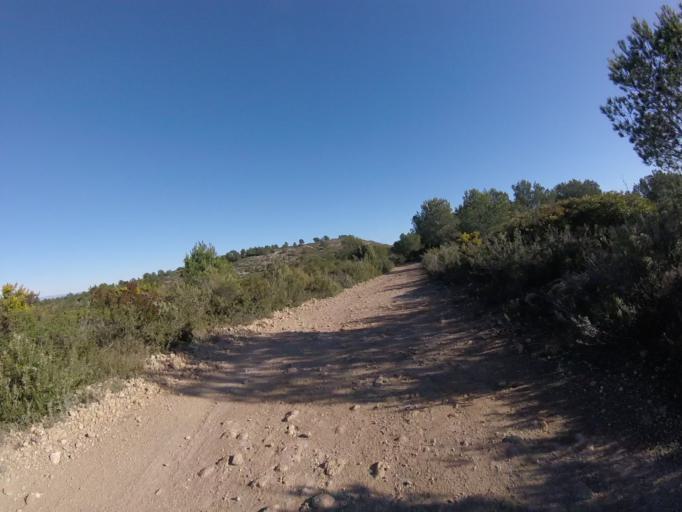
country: ES
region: Valencia
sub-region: Provincia de Castello
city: Orpesa/Oropesa del Mar
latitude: 40.0965
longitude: 0.1057
